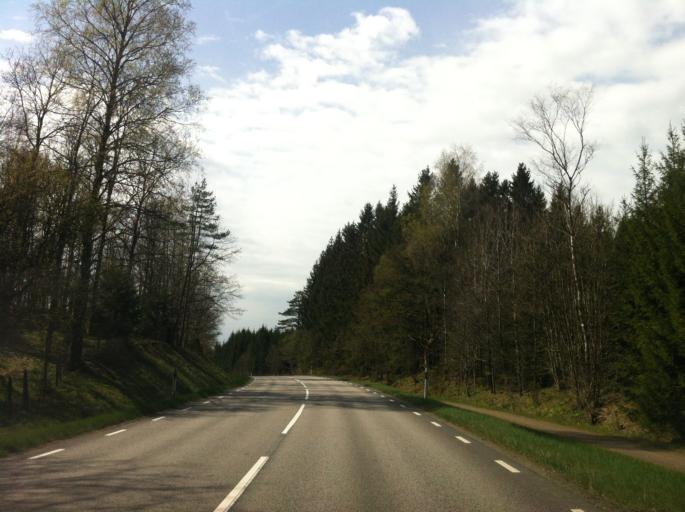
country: SE
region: Vaestra Goetaland
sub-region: Marks Kommun
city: Horred
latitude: 57.1528
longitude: 12.7303
